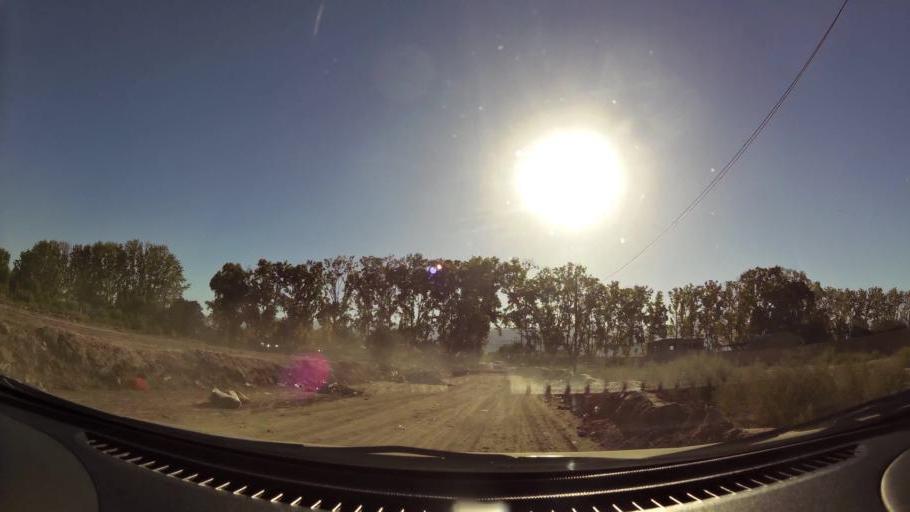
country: AR
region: Mendoza
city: Las Heras
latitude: -32.8475
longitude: -68.8264
